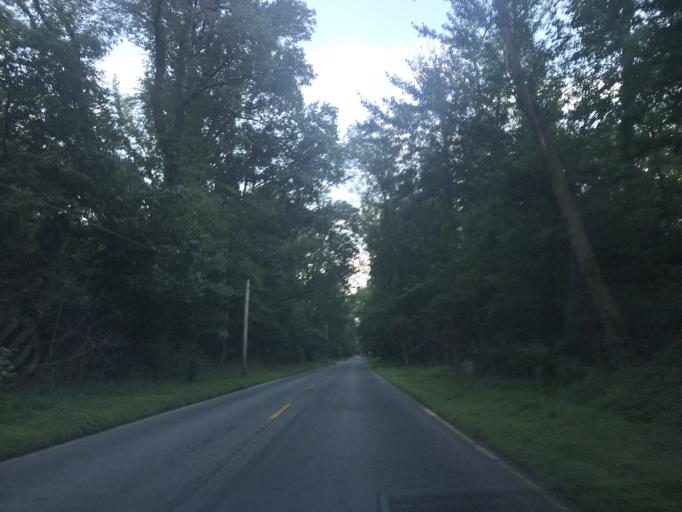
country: US
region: Maryland
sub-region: Cecil County
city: Rising Sun
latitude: 39.6396
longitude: -76.1495
